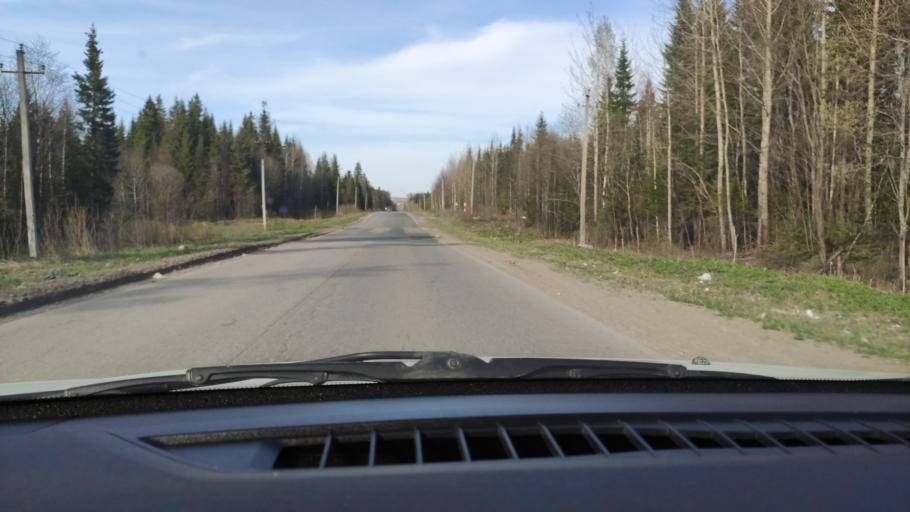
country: RU
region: Perm
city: Novyye Lyady
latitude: 57.9455
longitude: 56.5018
